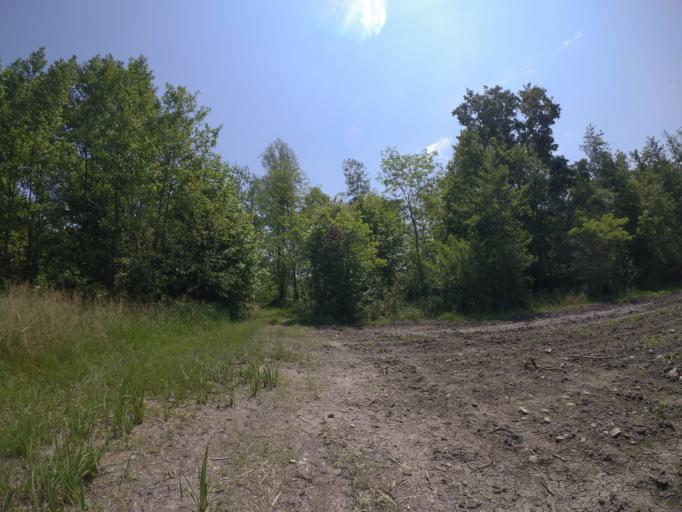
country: IT
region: Friuli Venezia Giulia
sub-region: Provincia di Udine
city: Bertiolo
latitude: 45.9141
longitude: 13.0310
